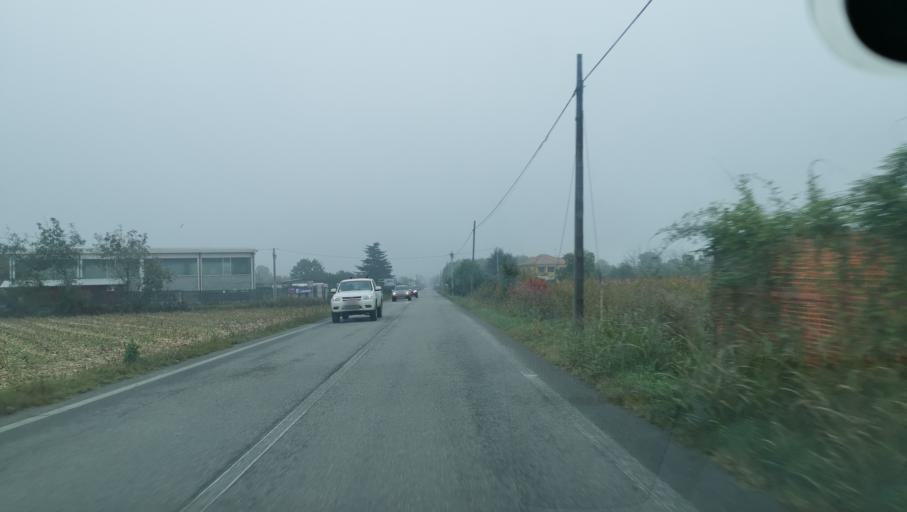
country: IT
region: Piedmont
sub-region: Provincia di Biella
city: Cavaglia
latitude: 45.3914
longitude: 8.0879
